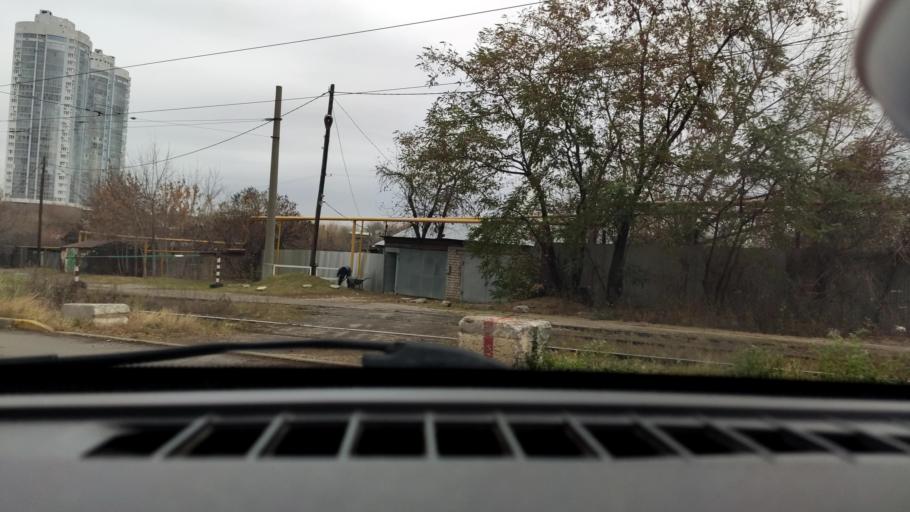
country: RU
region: Samara
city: Samara
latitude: 53.2187
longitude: 50.1712
